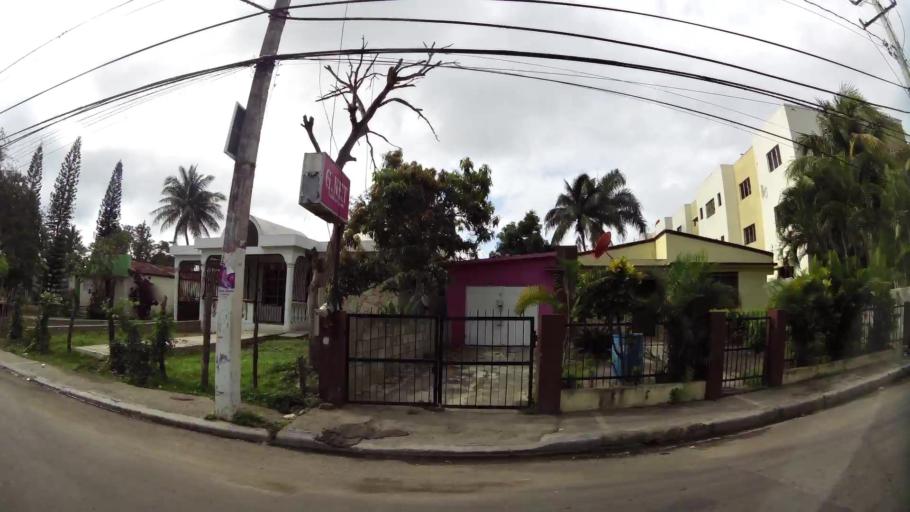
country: DO
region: Santiago
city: Santiago de los Caballeros
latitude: 19.4264
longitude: -70.6564
